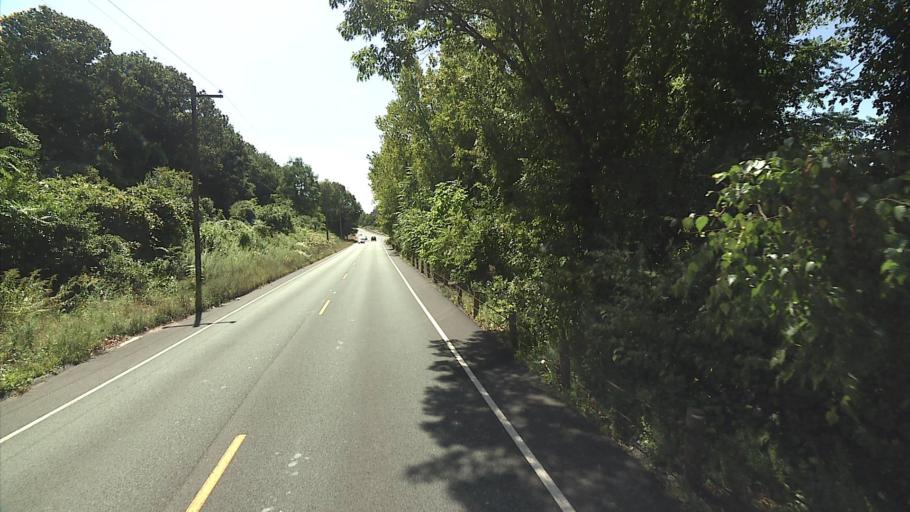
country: US
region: Connecticut
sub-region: New Haven County
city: Waterbury
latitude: 41.5714
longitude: -73.0532
